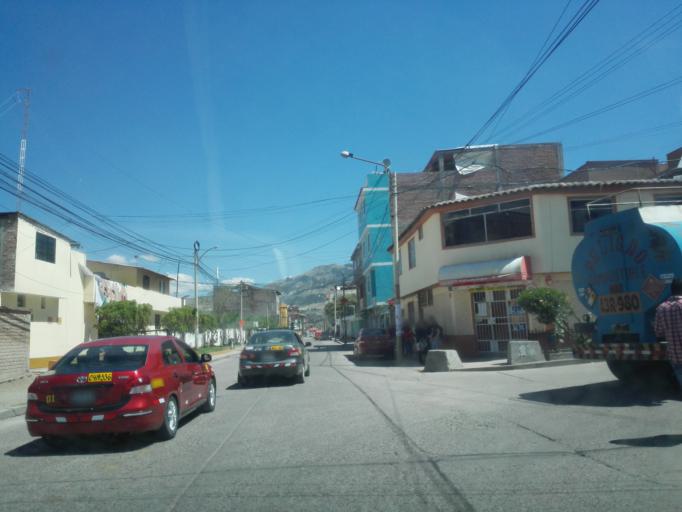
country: PE
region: Ayacucho
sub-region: Provincia de Huamanga
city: Ayacucho
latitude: -13.1529
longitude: -74.2274
